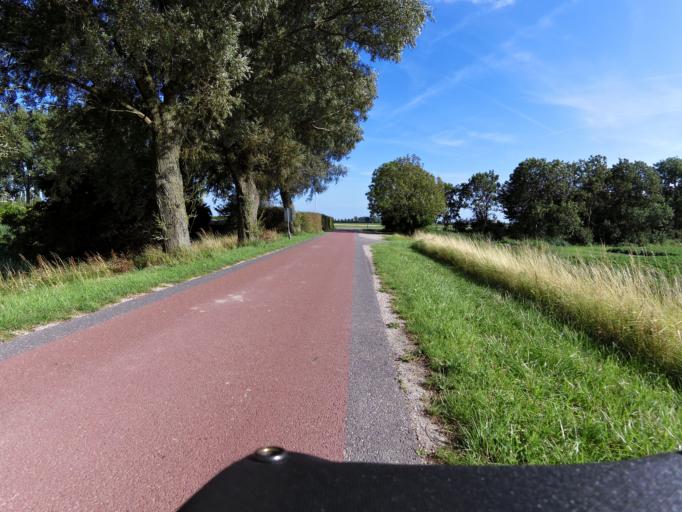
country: NL
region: South Holland
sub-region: Gemeente Goeree-Overflakkee
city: Dirksland
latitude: 51.7543
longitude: 4.1262
